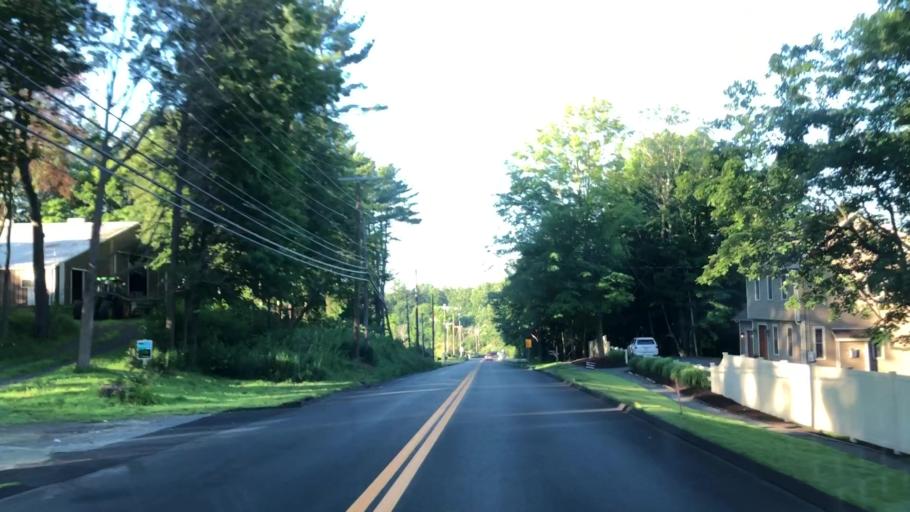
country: US
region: Massachusetts
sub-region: Hampshire County
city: Southampton
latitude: 42.2337
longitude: -72.7269
